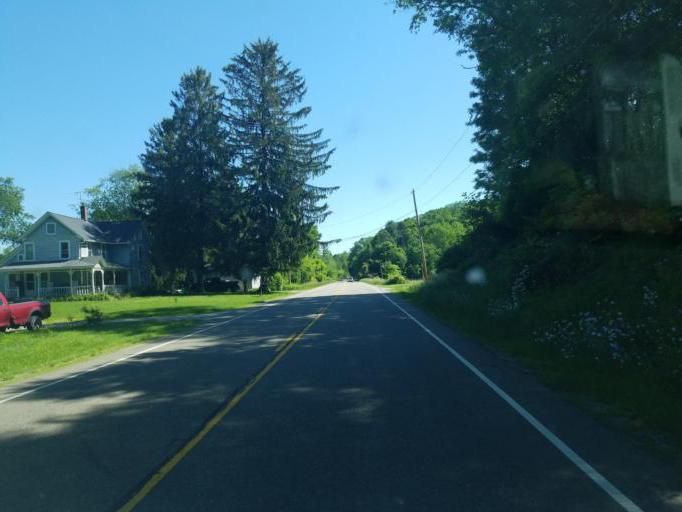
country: US
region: Ohio
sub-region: Summit County
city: Peninsula
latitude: 41.2051
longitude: -81.5628
